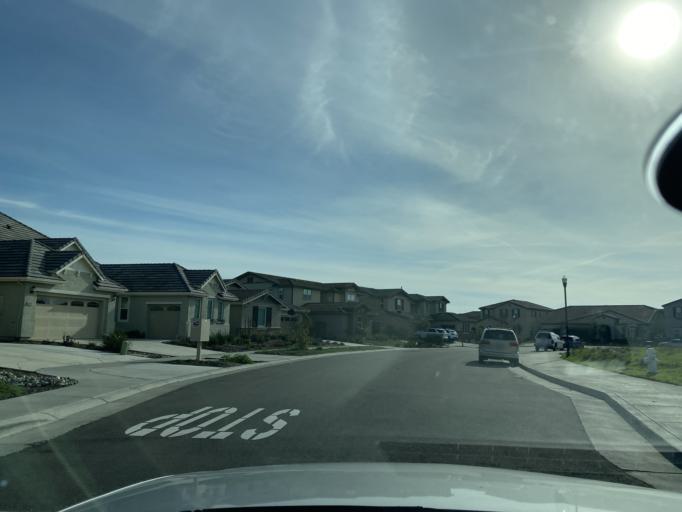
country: US
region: California
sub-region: Sacramento County
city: Elk Grove
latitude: 38.3984
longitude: -121.3889
